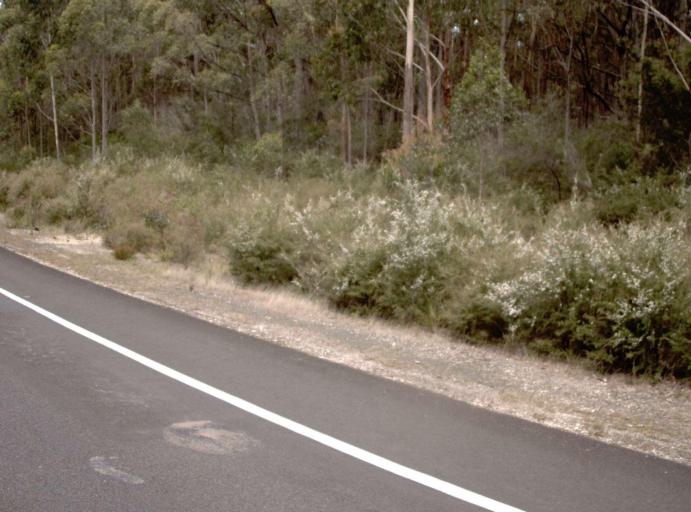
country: AU
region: New South Wales
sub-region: Bega Valley
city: Eden
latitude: -37.5089
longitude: 149.5171
